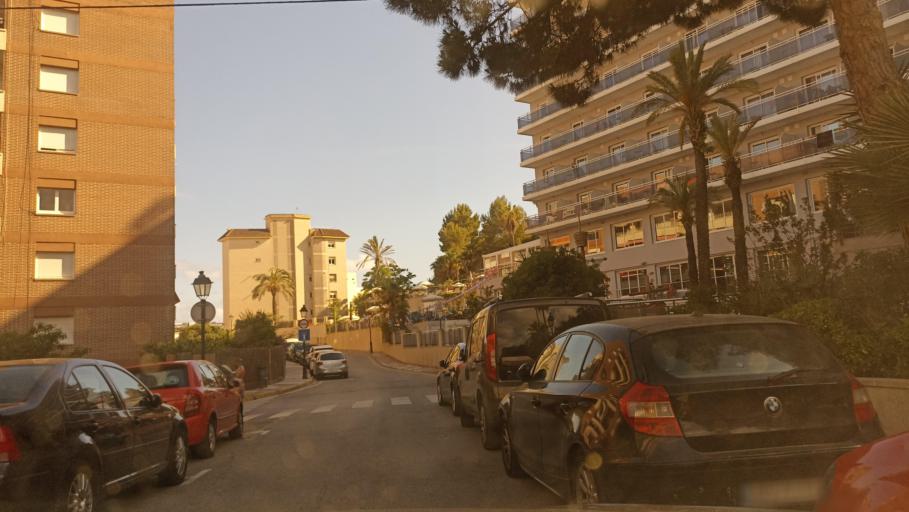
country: ES
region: Catalonia
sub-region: Provincia de Barcelona
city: Calella
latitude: 41.6133
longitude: 2.6499
